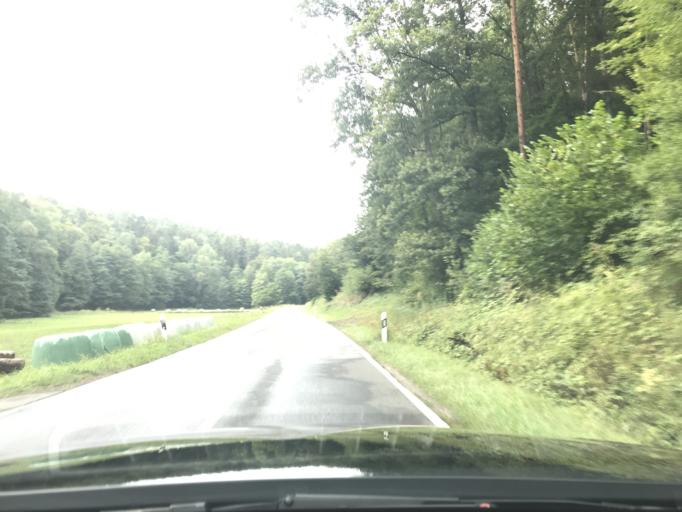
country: DE
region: Bavaria
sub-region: Regierungsbezirk Unterfranken
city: Breitbrunn
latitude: 50.0285
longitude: 10.6790
